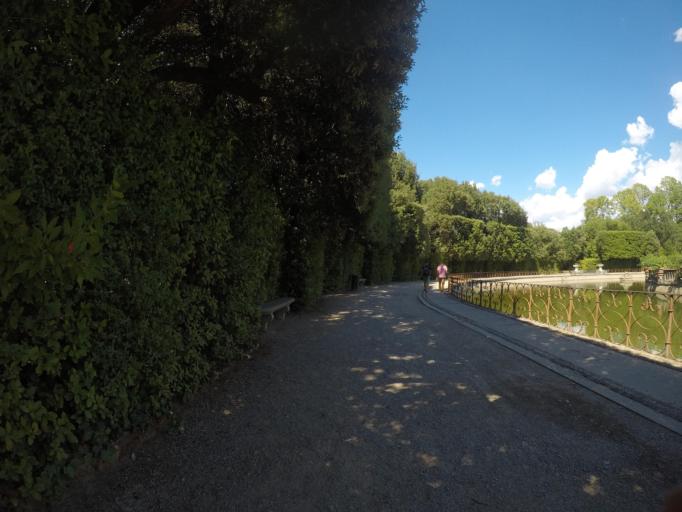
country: IT
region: Tuscany
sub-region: Province of Florence
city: Florence
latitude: 43.7615
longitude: 11.2451
